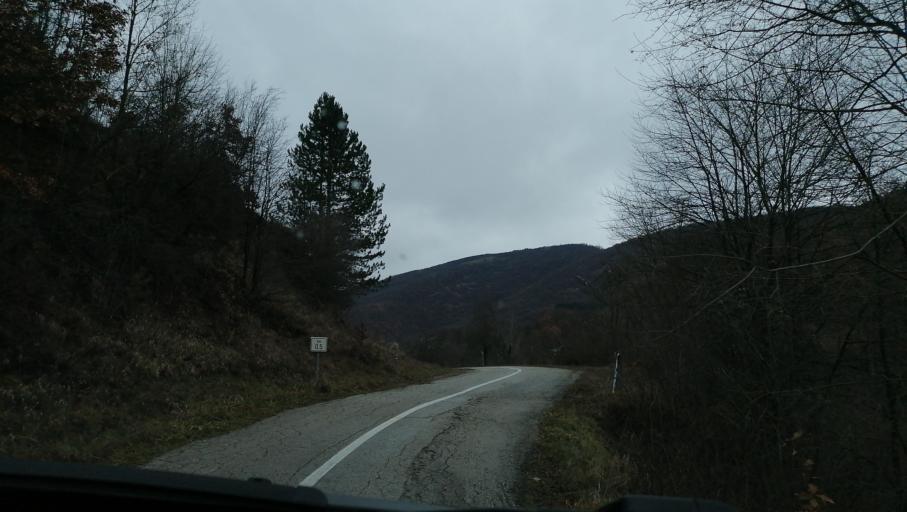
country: RS
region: Central Serbia
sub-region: Pirotski Okrug
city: Dimitrovgrad
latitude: 42.9768
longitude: 22.7841
